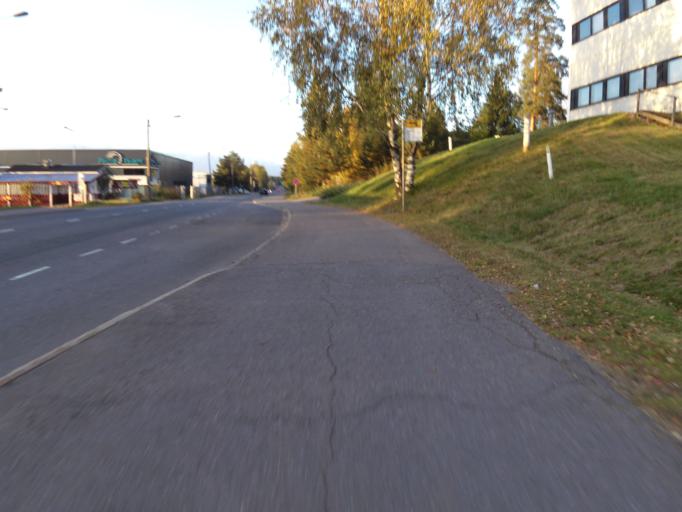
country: FI
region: Uusimaa
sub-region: Helsinki
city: Kilo
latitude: 60.2748
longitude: 24.7610
